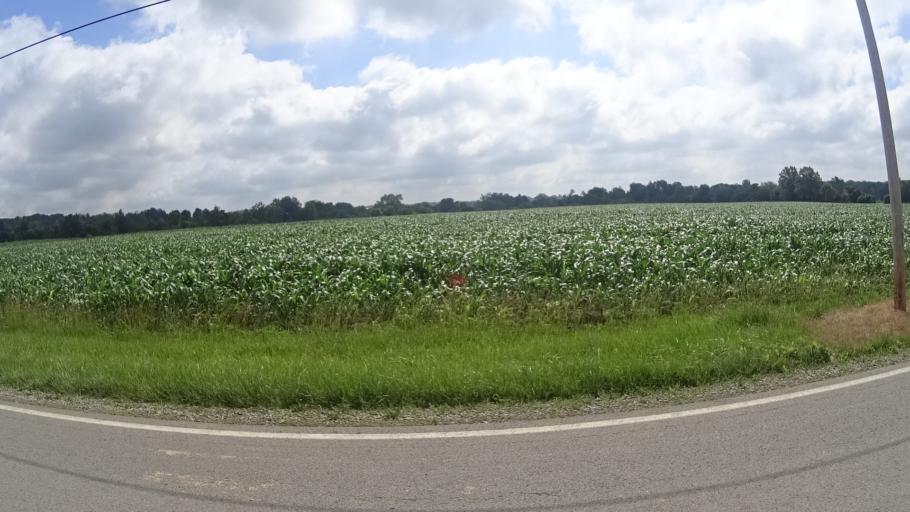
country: US
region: Ohio
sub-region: Huron County
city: Wakeman
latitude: 41.3046
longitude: -82.4133
